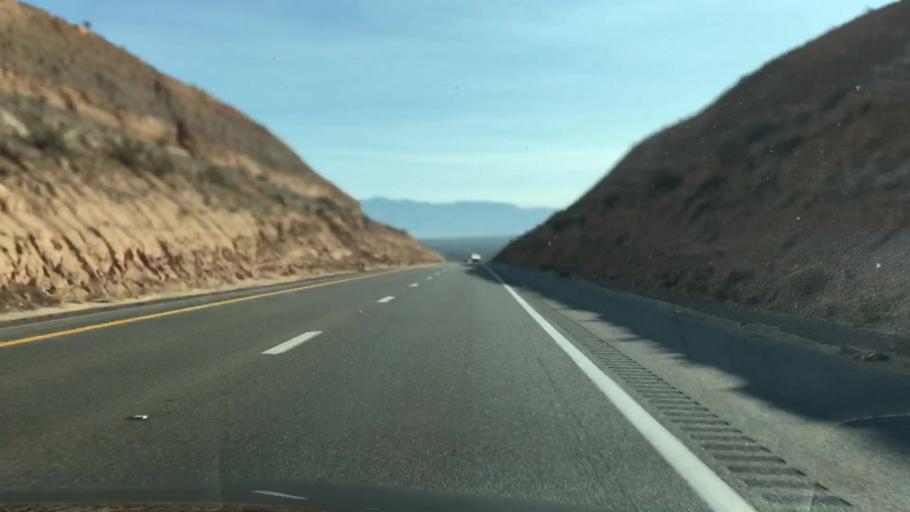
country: US
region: Nevada
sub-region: Clark County
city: Bunkerville
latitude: 36.7668
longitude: -114.2077
